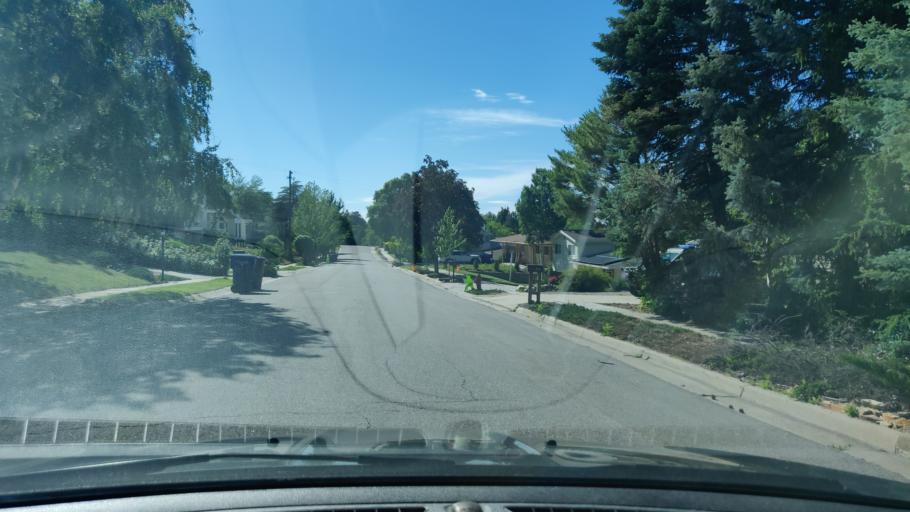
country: US
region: Utah
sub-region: Salt Lake County
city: Cottonwood Heights
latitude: 40.6171
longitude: -111.7936
